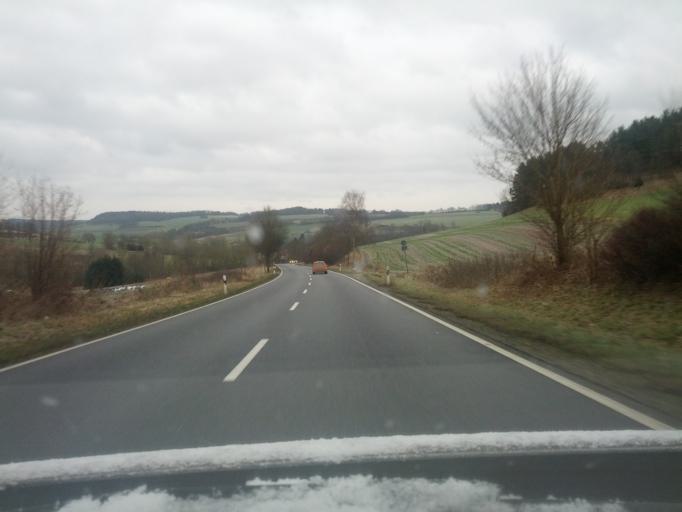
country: DE
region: Hesse
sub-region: Regierungsbezirk Kassel
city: Nentershausen
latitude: 51.0358
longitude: 10.0101
